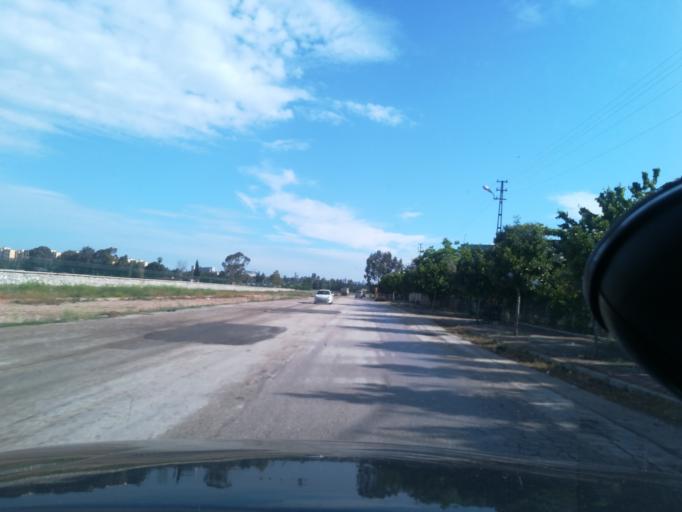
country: TR
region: Adana
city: Adana
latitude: 37.0181
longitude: 35.3626
